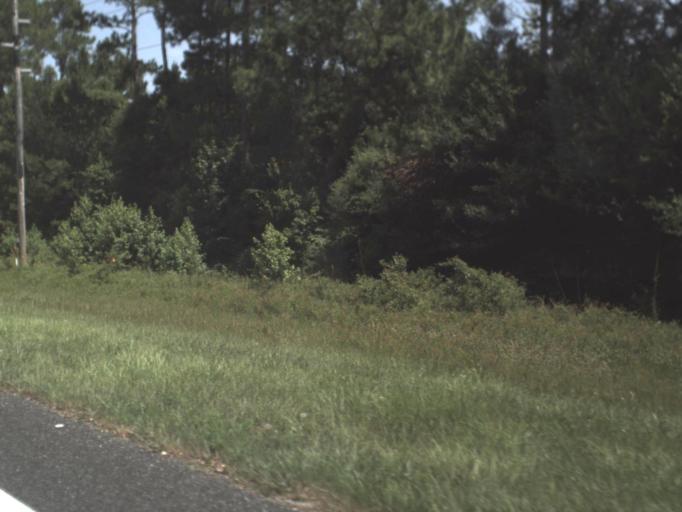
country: US
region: Florida
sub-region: Taylor County
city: Steinhatchee
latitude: 29.6919
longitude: -83.2737
